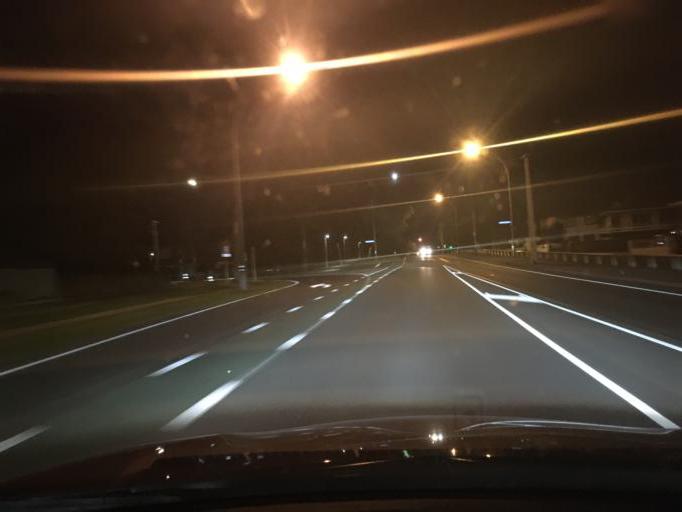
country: NZ
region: Waikato
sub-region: Hamilton City
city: Hamilton
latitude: -37.8226
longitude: 175.2886
